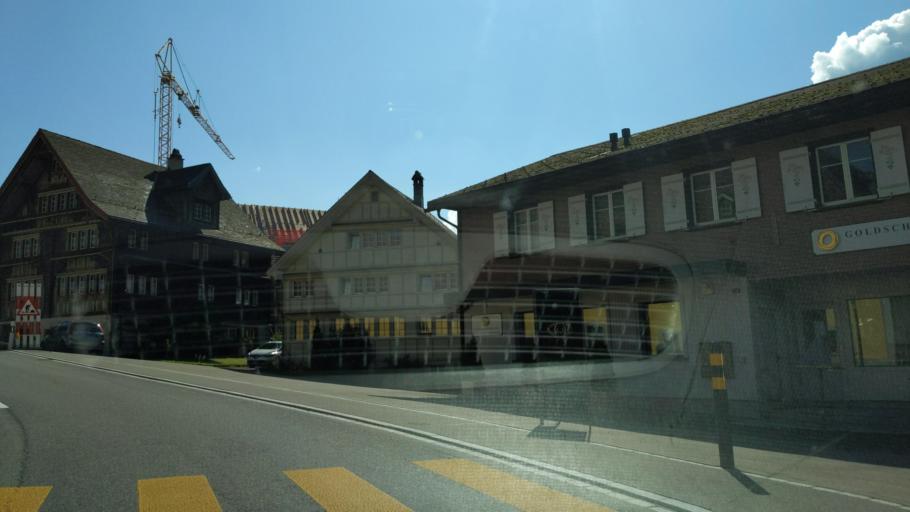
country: CH
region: Saint Gallen
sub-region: Wahlkreis Toggenburg
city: Sankt Peterzell
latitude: 47.3176
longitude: 9.1736
